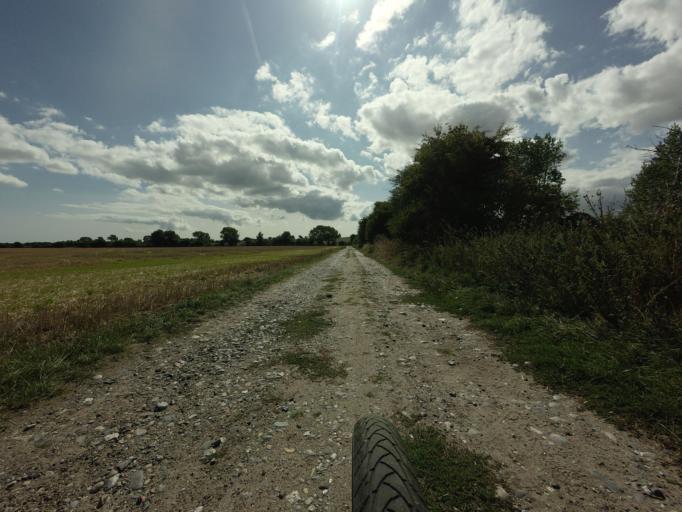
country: DK
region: Zealand
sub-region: Vordingborg Kommune
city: Stege
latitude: 55.0184
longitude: 12.4290
